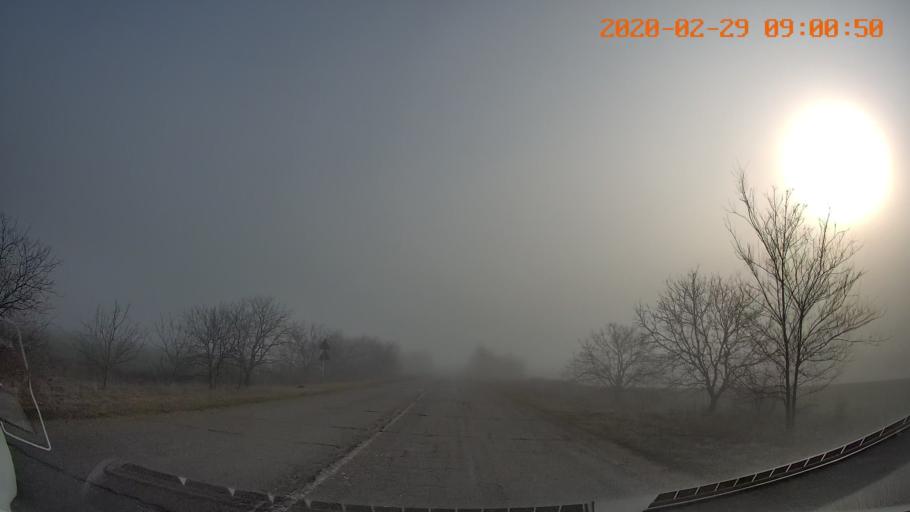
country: UA
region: Odessa
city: Velykoploske
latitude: 46.9229
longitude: 29.6826
